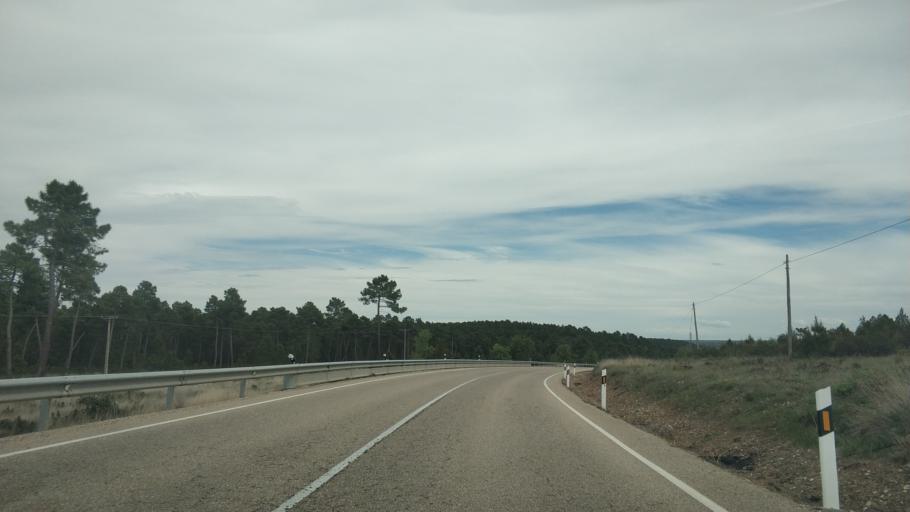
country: ES
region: Castille and Leon
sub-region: Provincia de Soria
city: Bayubas de Abajo
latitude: 41.5201
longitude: -2.9325
